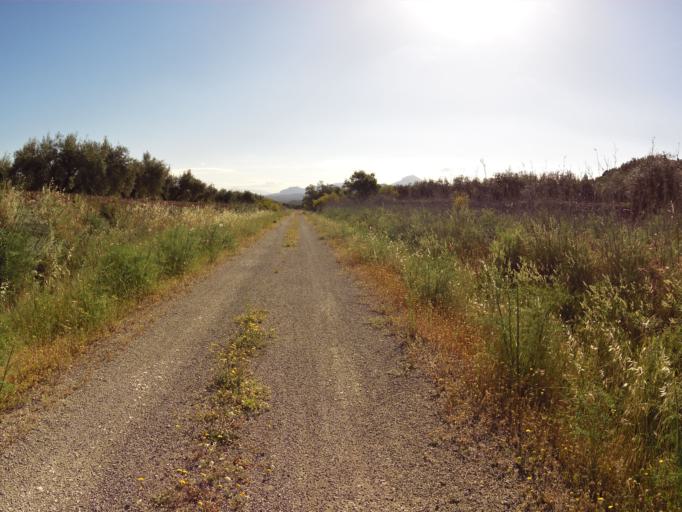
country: ES
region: Andalusia
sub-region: Province of Cordoba
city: Fuente-Tojar
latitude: 37.5821
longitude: -4.1940
